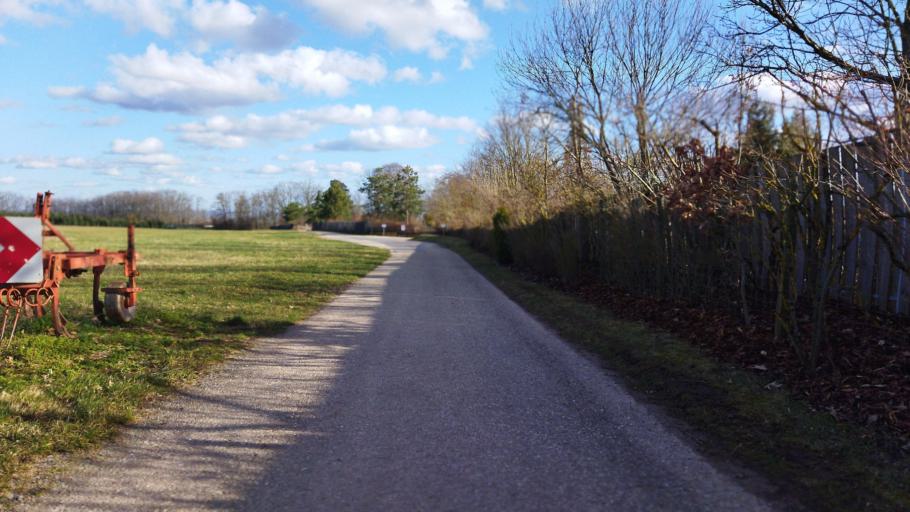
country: DE
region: Baden-Wuerttemberg
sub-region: Regierungsbezirk Stuttgart
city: Guglingen
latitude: 49.0905
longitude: 9.0063
